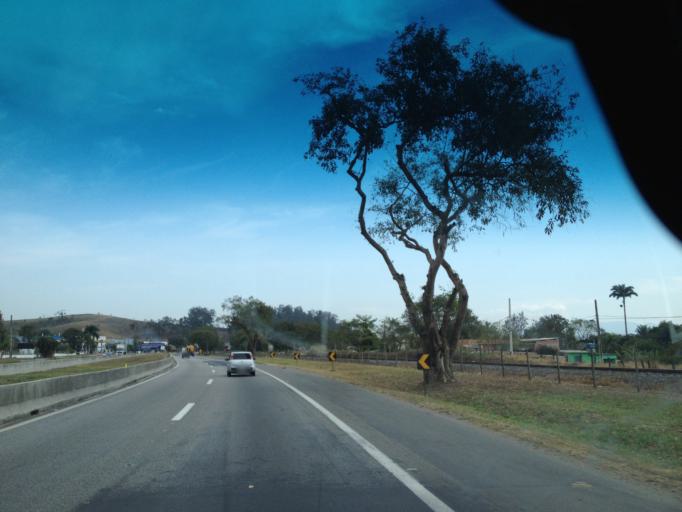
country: BR
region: Rio de Janeiro
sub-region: Porto Real
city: Porto Real
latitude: -22.4653
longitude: -44.2843
